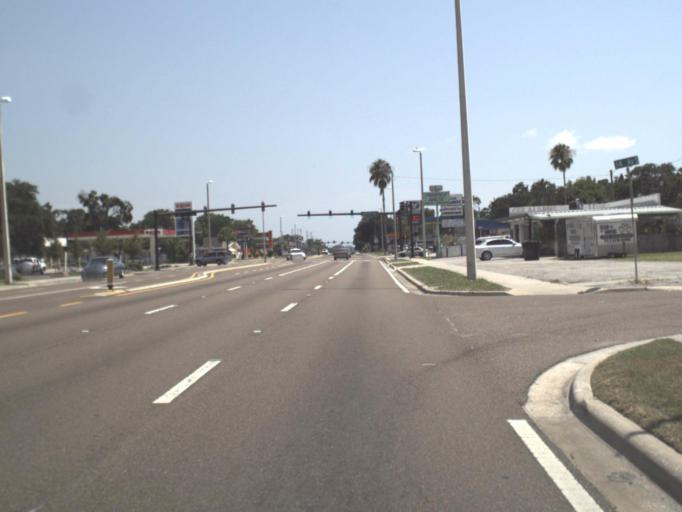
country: US
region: Florida
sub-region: Pinellas County
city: Saint Petersburg
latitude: 27.7567
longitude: -82.6795
